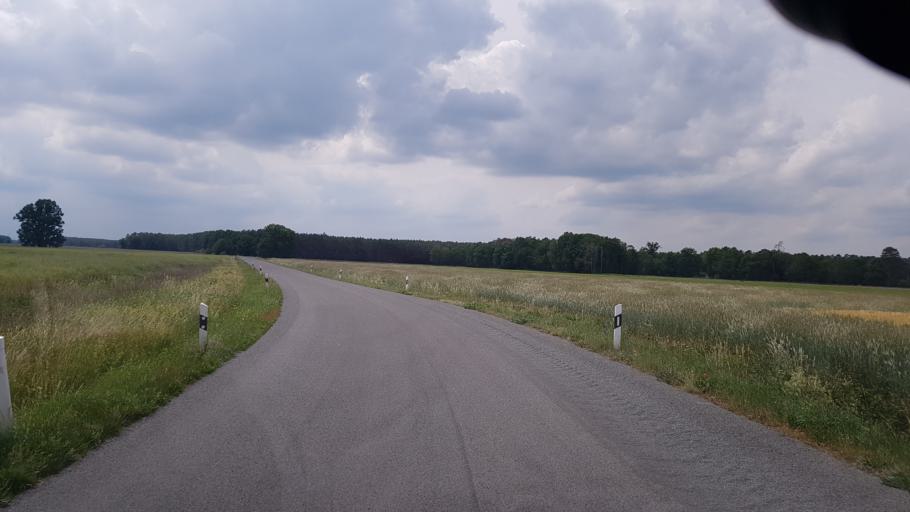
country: DE
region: Brandenburg
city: Ihlow
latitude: 51.8670
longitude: 13.3208
